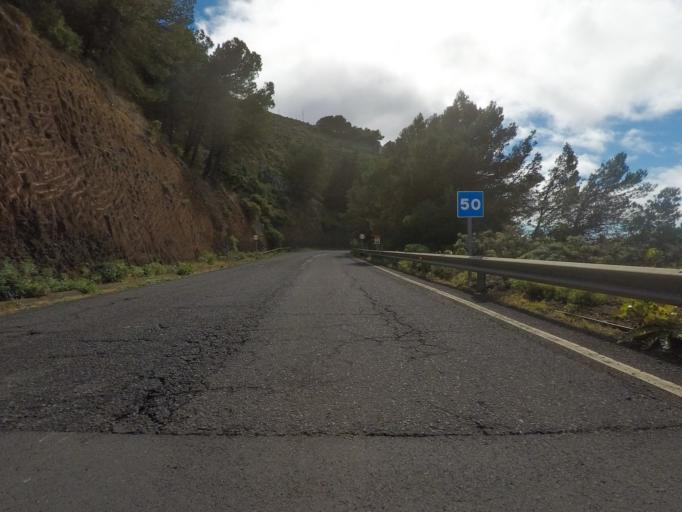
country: ES
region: Canary Islands
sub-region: Provincia de Santa Cruz de Tenerife
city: Vallehermosa
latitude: 28.1304
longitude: -17.3205
